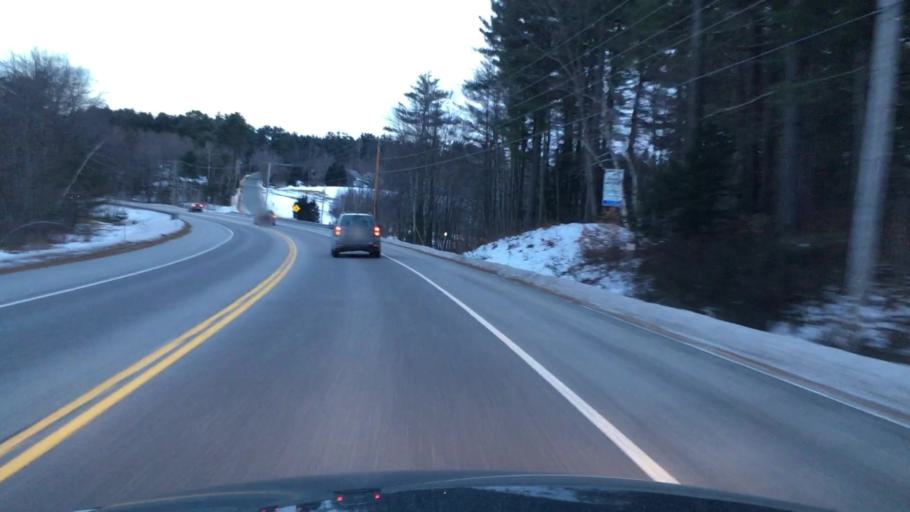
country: US
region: New Hampshire
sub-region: Merrimack County
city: Newbury
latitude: 43.2917
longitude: -71.9934
